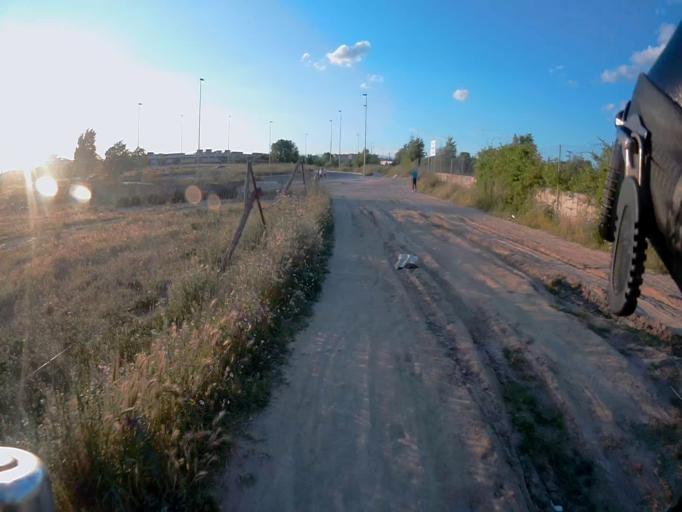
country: ES
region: Madrid
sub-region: Provincia de Madrid
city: Alcorcon
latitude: 40.3275
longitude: -3.8181
